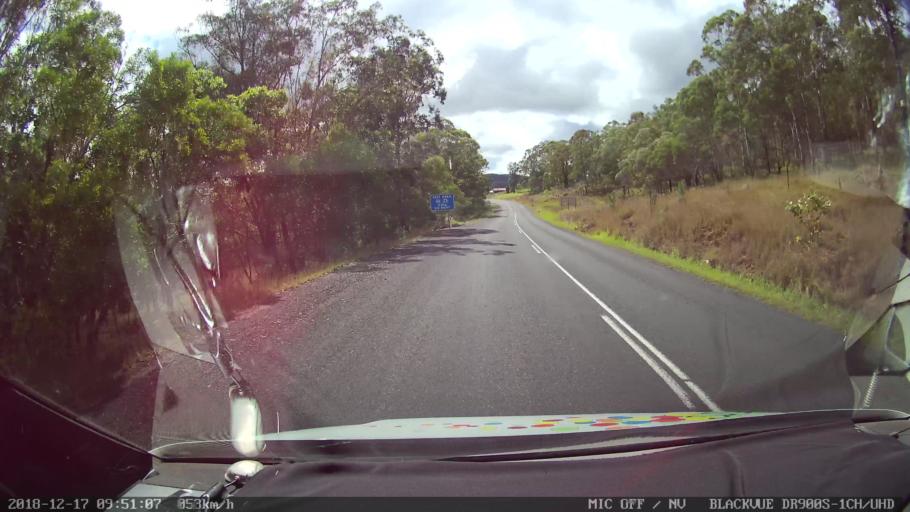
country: AU
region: New South Wales
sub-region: Tenterfield Municipality
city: Carrolls Creek
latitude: -28.9259
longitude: 152.3706
